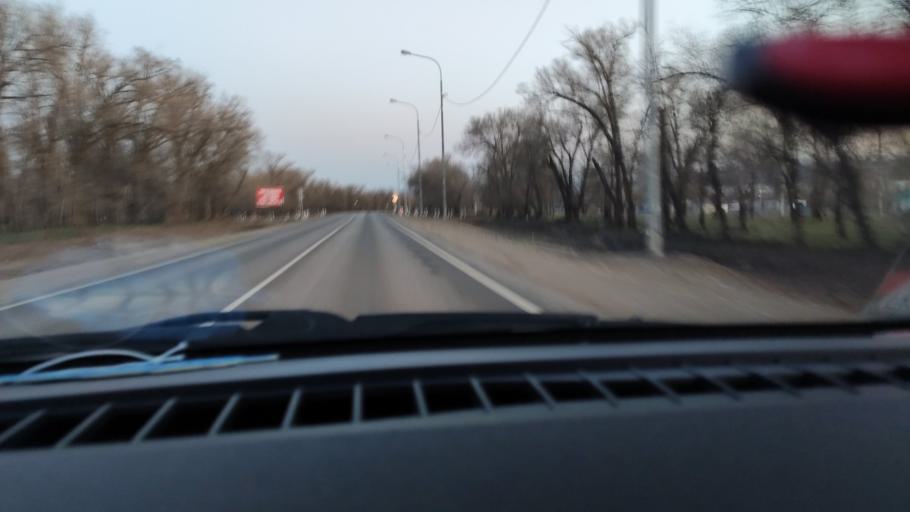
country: RU
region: Saratov
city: Krasnoarmeysk
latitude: 51.0859
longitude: 45.9577
